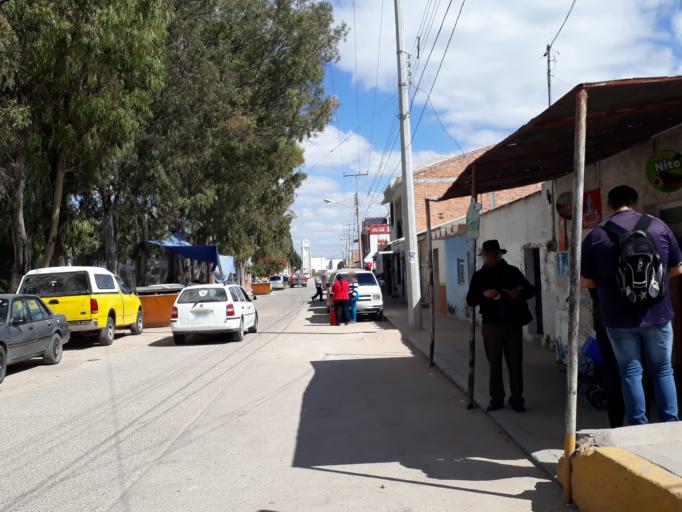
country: MX
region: Aguascalientes
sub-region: Aguascalientes
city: San Sebastian [Fraccionamiento]
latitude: 21.8004
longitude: -102.2743
